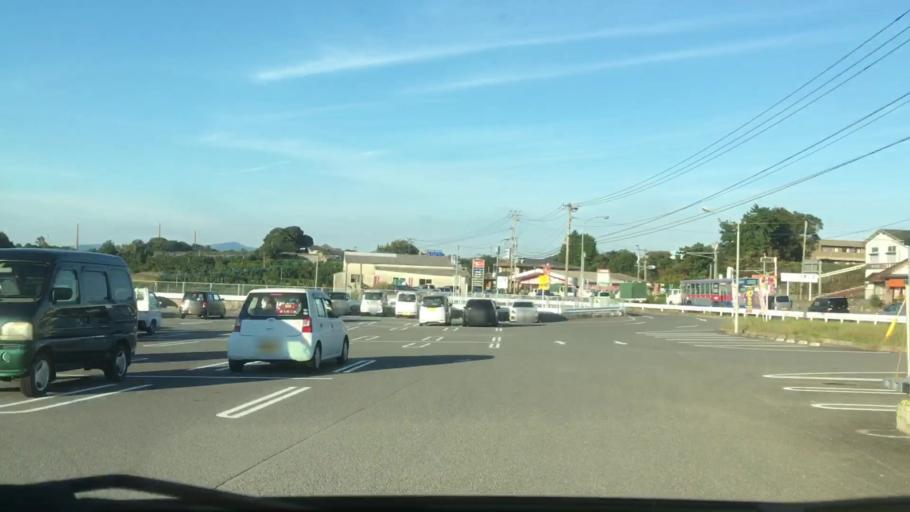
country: JP
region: Nagasaki
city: Sasebo
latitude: 33.0444
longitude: 129.7441
